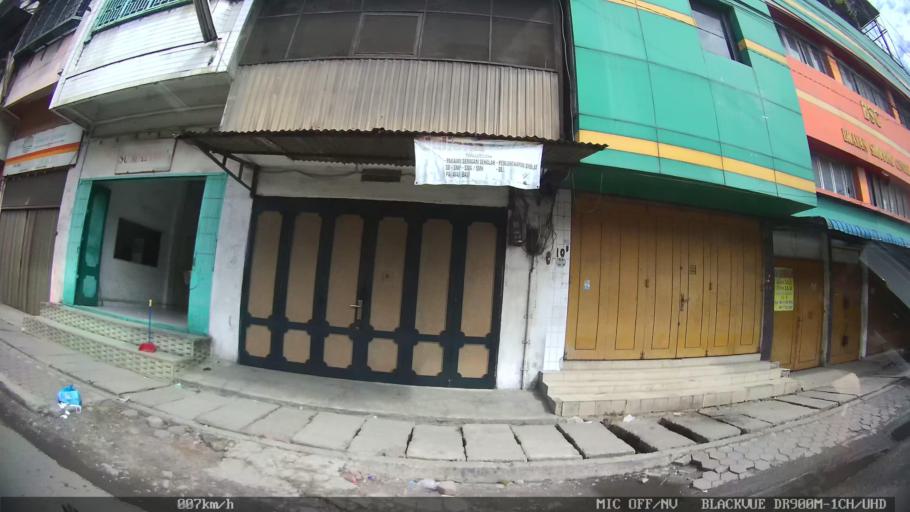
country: ID
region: North Sumatra
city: Medan
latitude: 3.6280
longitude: 98.6681
